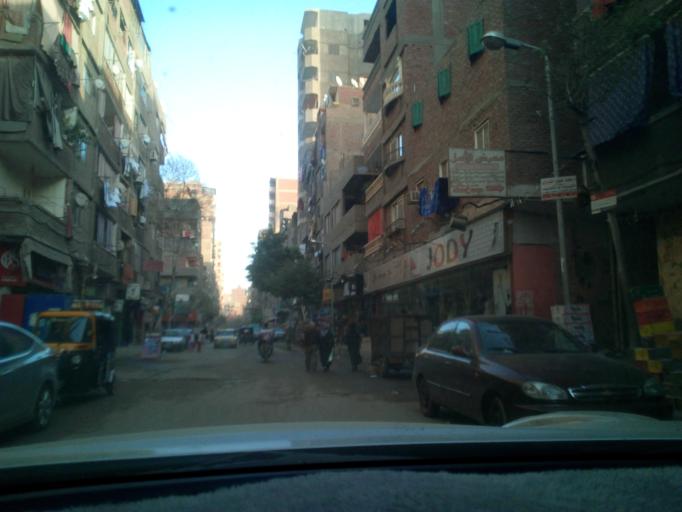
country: EG
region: Muhafazat al Qalyubiyah
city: Al Khankah
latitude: 30.1309
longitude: 31.3419
